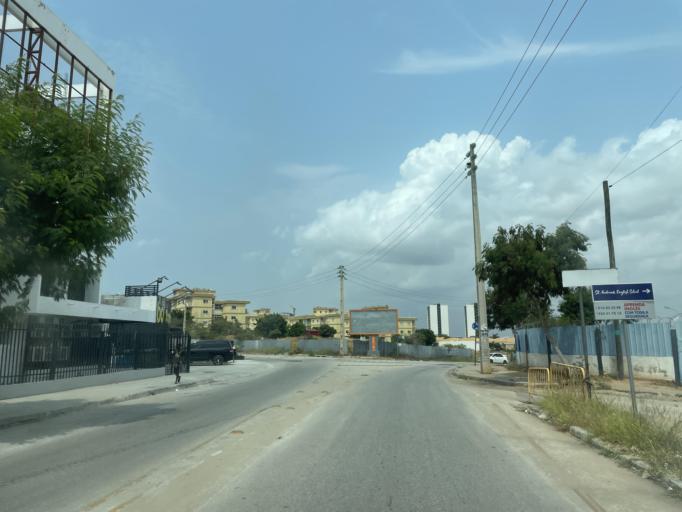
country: AO
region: Luanda
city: Luanda
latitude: -8.9231
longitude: 13.1955
